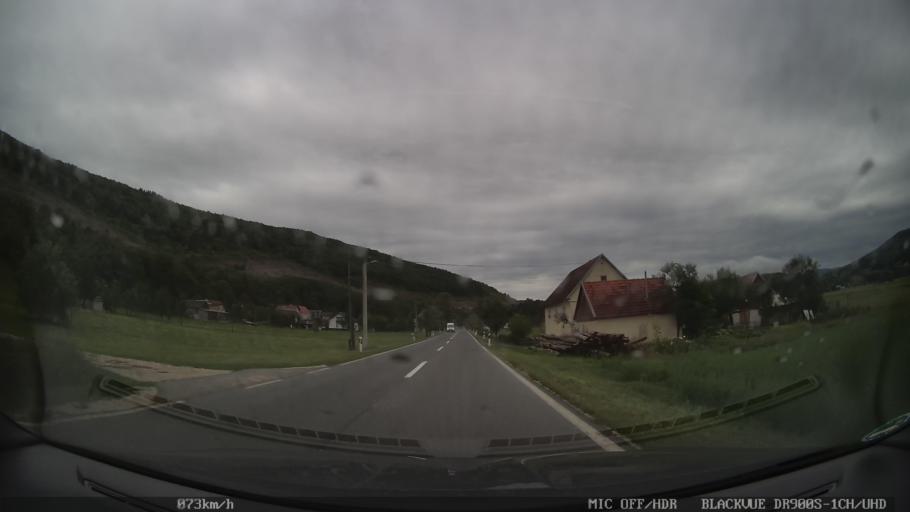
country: HR
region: Licko-Senjska
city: Otocac
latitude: 44.9026
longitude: 15.1768
